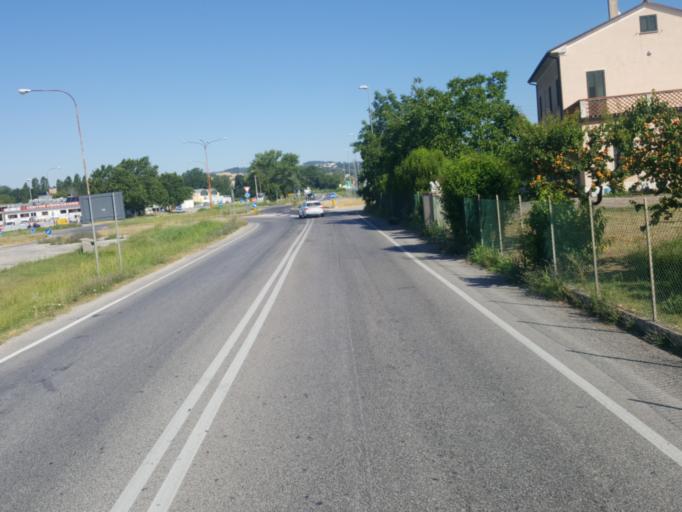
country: IT
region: The Marches
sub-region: Provincia di Pesaro e Urbino
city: Borgo Santa Maria
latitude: 43.8631
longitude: 12.8155
